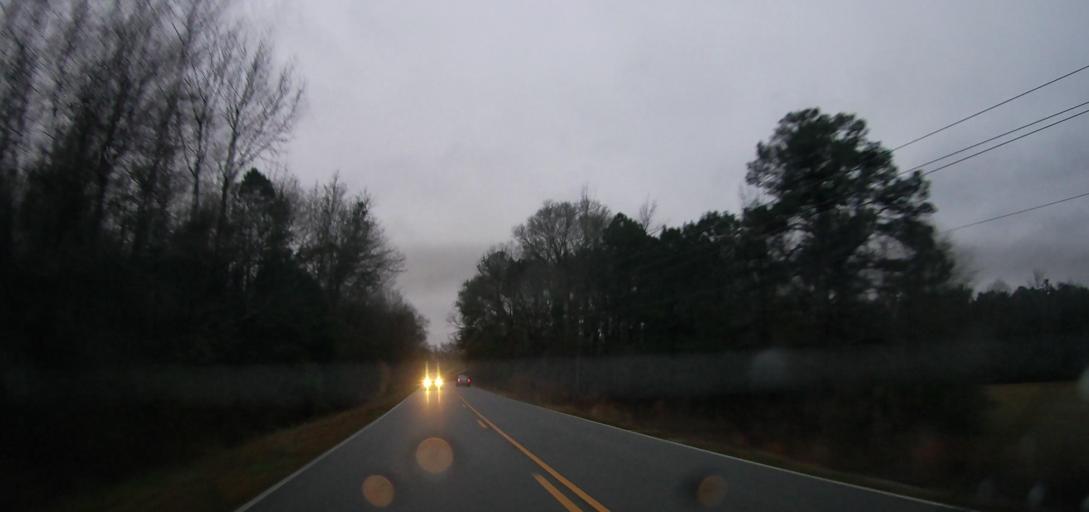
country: US
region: Alabama
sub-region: Tuscaloosa County
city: Vance
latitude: 33.1230
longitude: -87.2266
